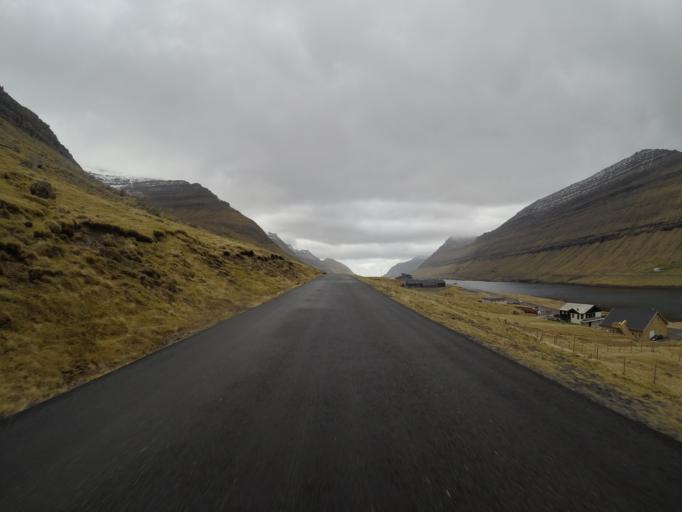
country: FO
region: Nordoyar
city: Klaksvik
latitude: 62.2983
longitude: -6.5305
